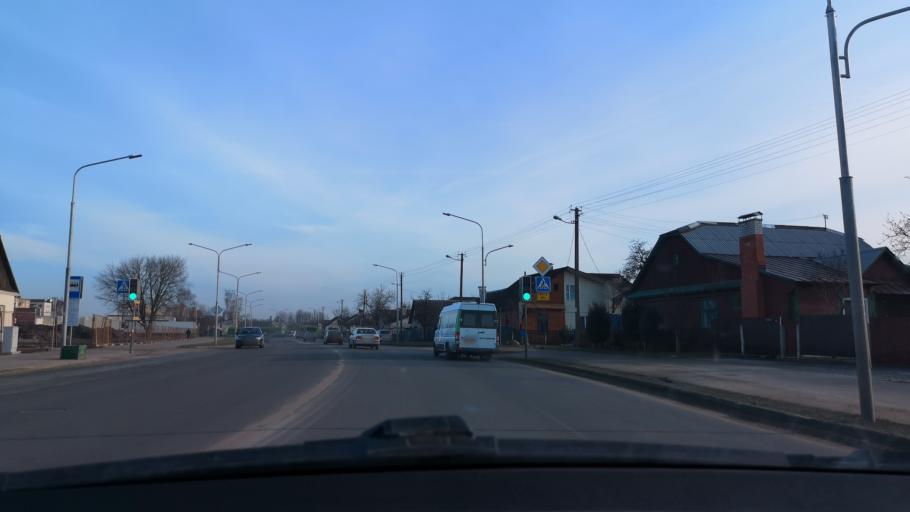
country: BY
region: Brest
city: Brest
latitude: 52.1038
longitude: 23.6677
